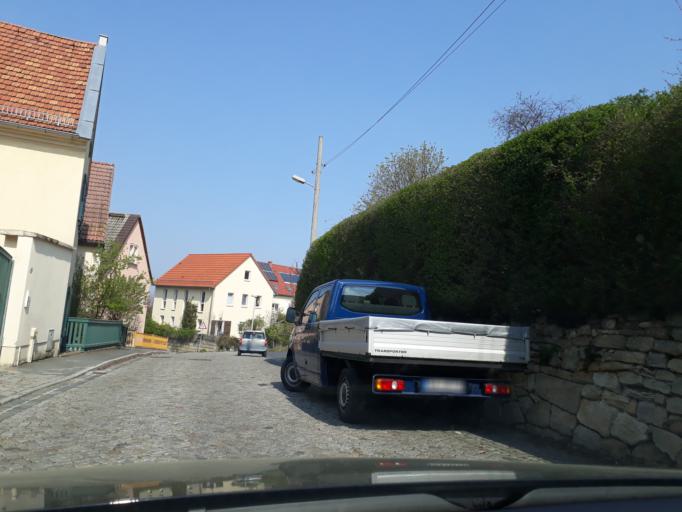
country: DE
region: Saxony
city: Bannewitz
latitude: 51.0099
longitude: 13.7492
